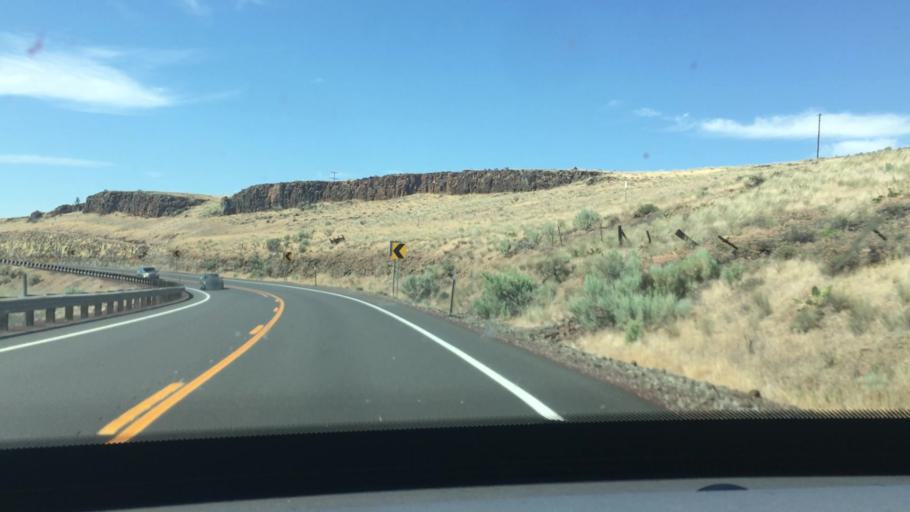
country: US
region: Oregon
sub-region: Sherman County
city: Moro
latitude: 45.0998
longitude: -120.6761
